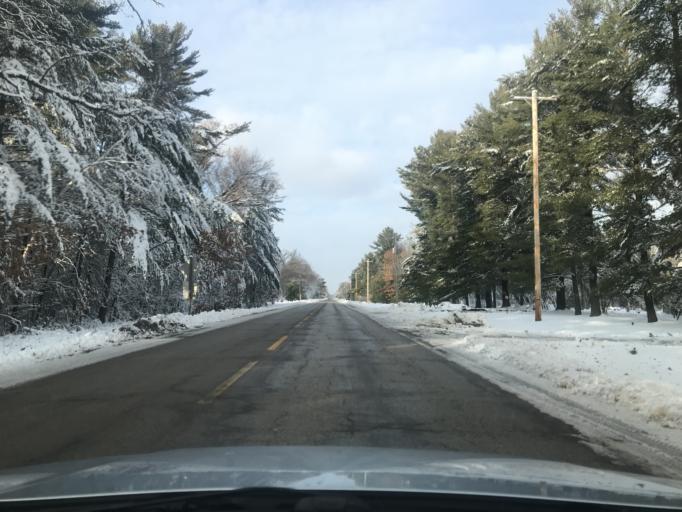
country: US
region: Wisconsin
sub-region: Marinette County
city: Peshtigo
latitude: 45.0657
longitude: -87.7400
